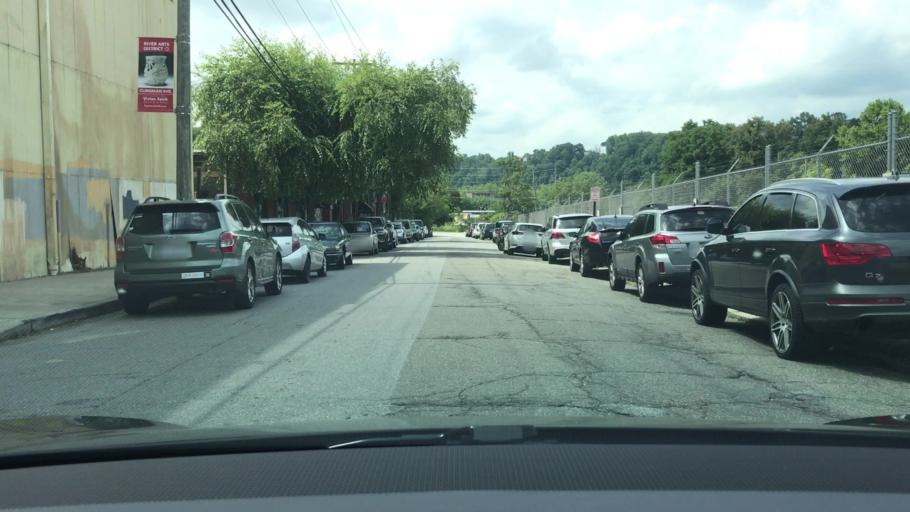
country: US
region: North Carolina
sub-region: Buncombe County
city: Asheville
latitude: 35.5860
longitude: -82.5644
